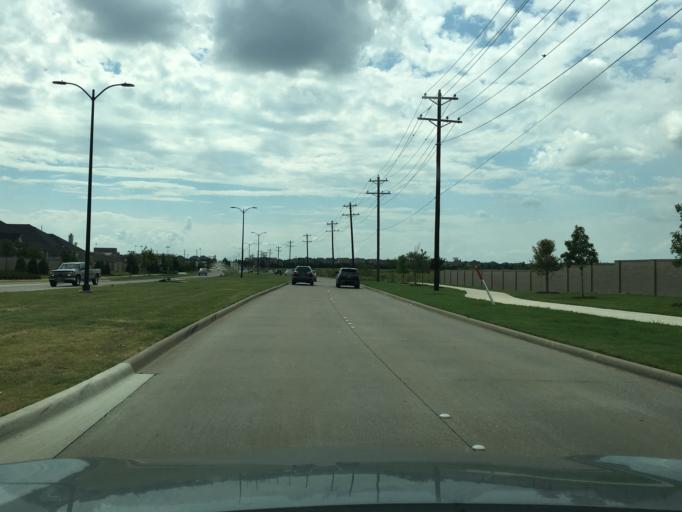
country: US
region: Texas
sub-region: Collin County
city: Frisco
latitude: 33.1329
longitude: -96.8536
